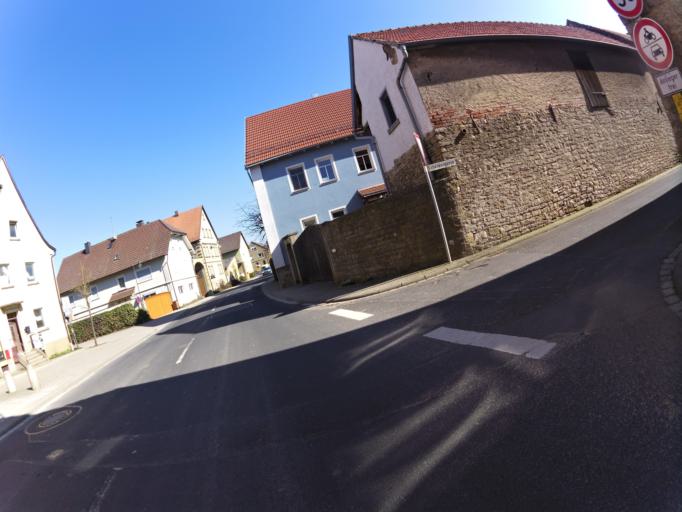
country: DE
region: Bavaria
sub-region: Regierungsbezirk Unterfranken
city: Oberpleichfeld
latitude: 49.8788
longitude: 10.0857
